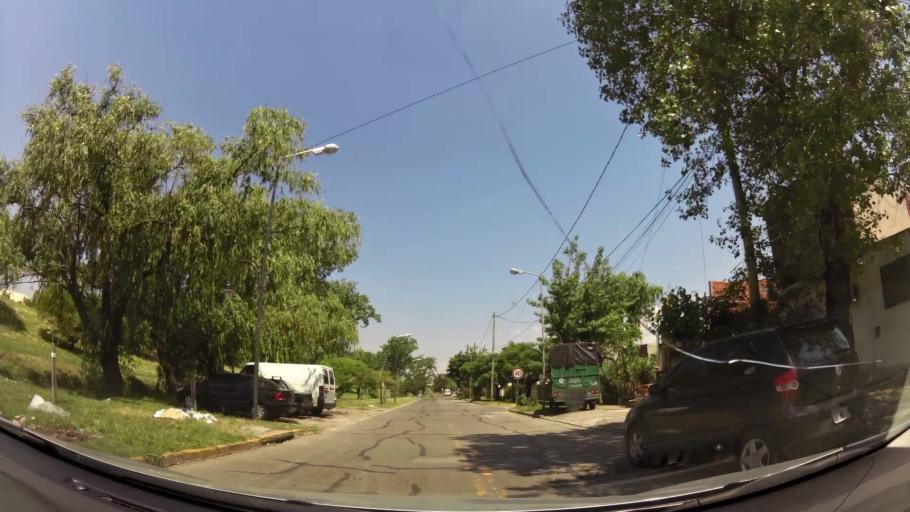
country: AR
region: Buenos Aires
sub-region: Partido de Tigre
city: Tigre
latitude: -34.4456
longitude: -58.5797
